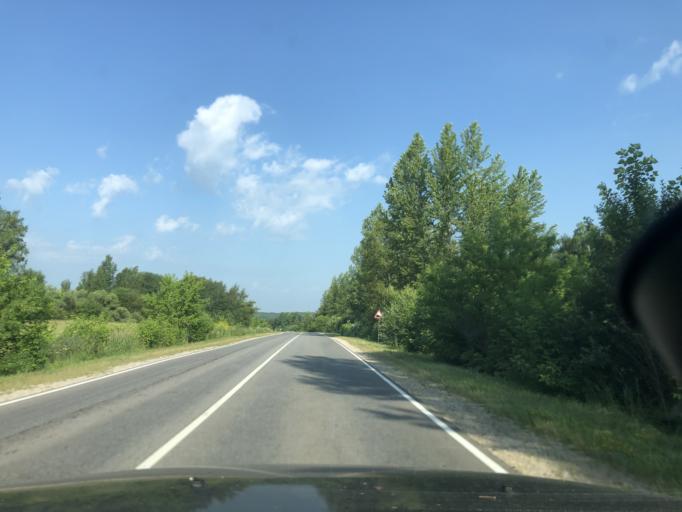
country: RU
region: Tula
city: Dubna
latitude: 54.1258
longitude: 37.0658
